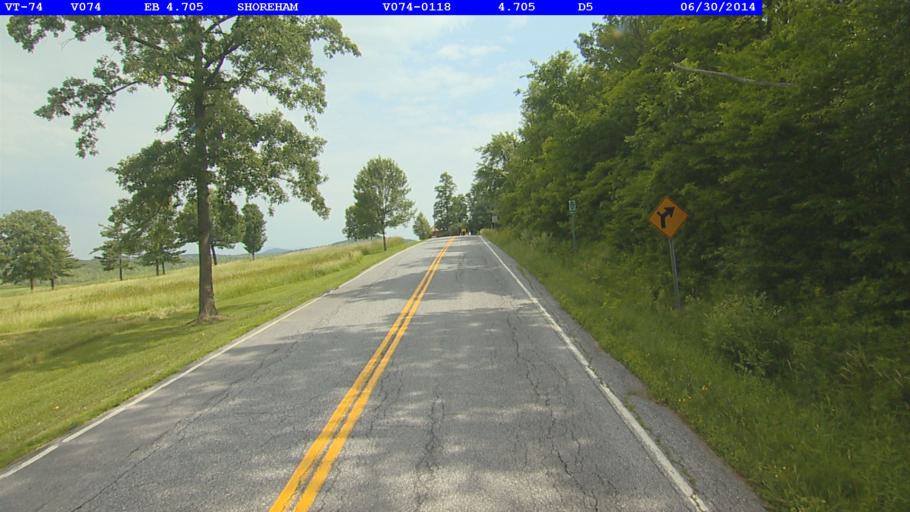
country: US
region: New York
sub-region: Essex County
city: Ticonderoga
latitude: 43.8922
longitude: -73.3187
